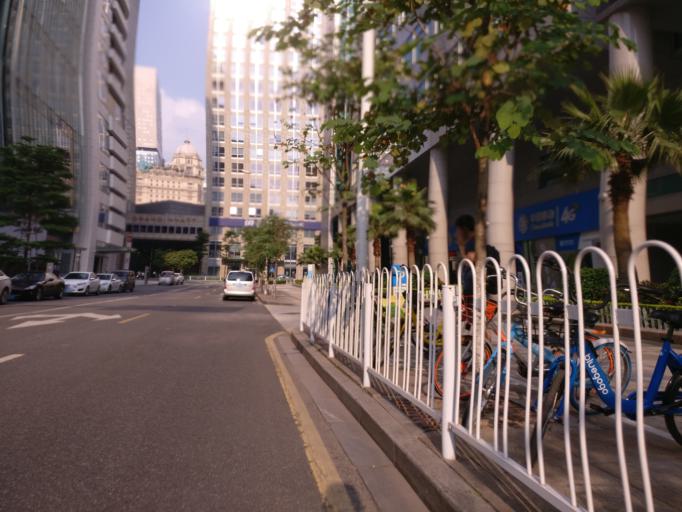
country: CN
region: Guangdong
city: Wushan
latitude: 23.1248
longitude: 113.3165
